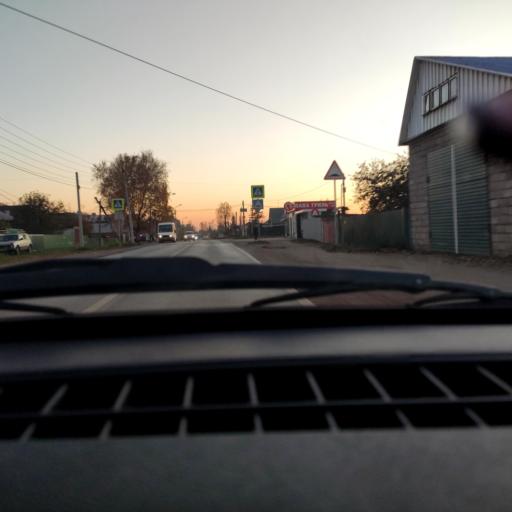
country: RU
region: Bashkortostan
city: Ufa
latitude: 54.8195
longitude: 56.1715
